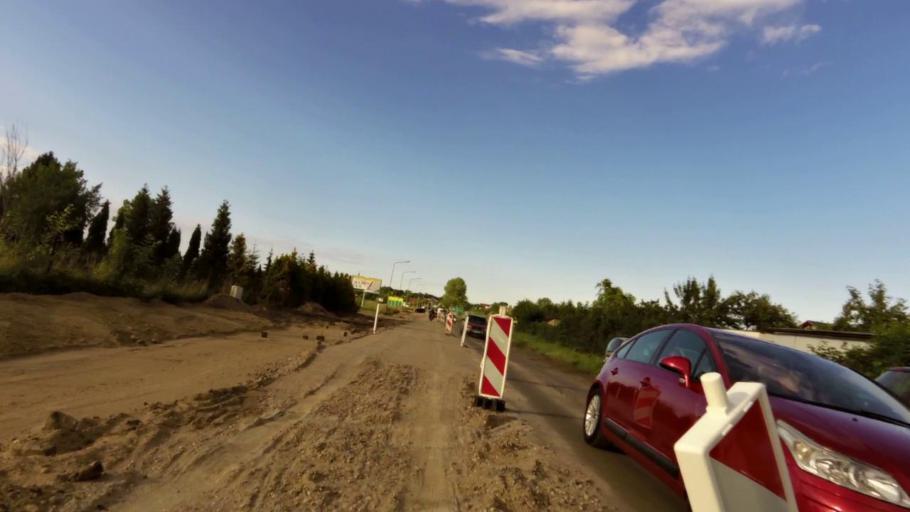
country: PL
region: West Pomeranian Voivodeship
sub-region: Powiat slawienski
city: Darlowo
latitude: 54.4123
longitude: 16.3975
